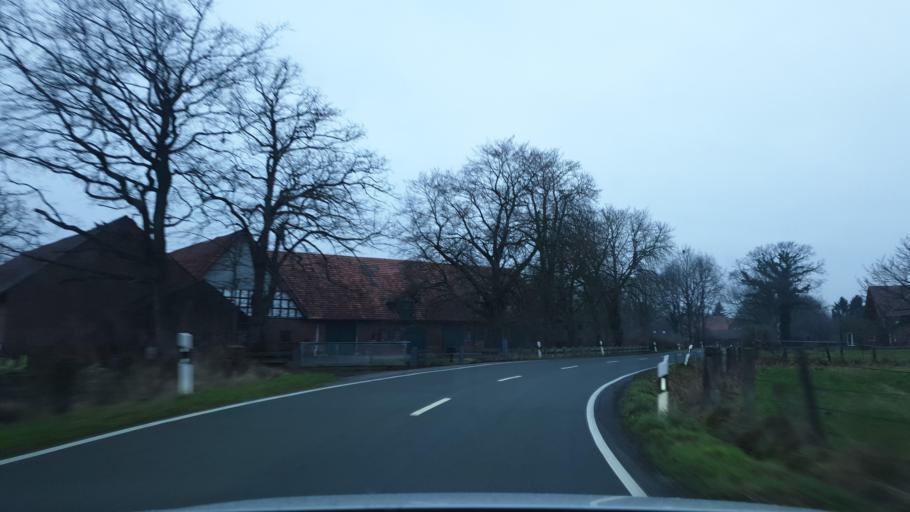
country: DE
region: North Rhine-Westphalia
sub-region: Regierungsbezirk Detmold
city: Petershagen
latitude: 52.3672
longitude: 8.8885
